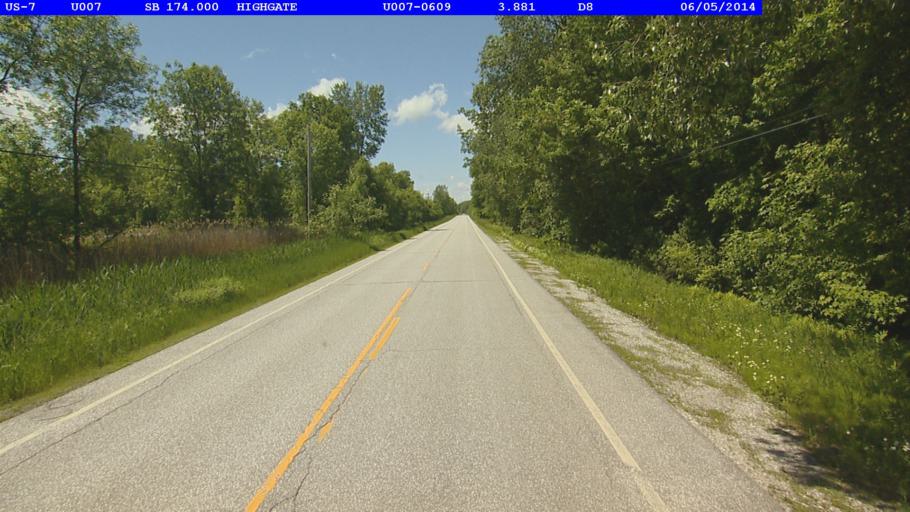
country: US
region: Vermont
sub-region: Franklin County
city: Swanton
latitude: 44.9842
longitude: -73.0922
